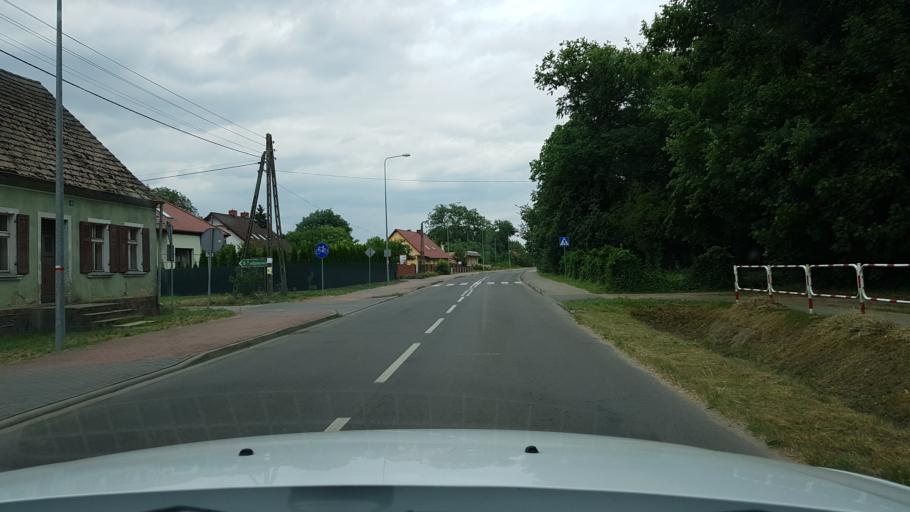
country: PL
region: Lubusz
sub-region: Powiat gorzowski
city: Kostrzyn nad Odra
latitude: 52.6231
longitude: 14.5820
